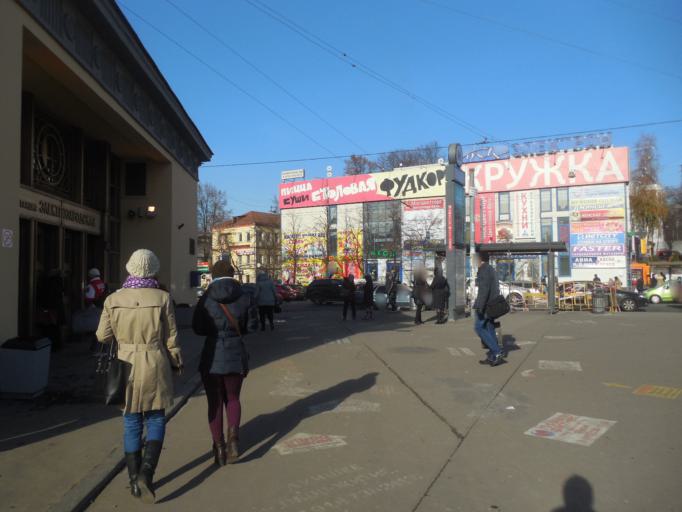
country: RU
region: Moscow
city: Lefortovo
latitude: 55.7820
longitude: 37.7056
